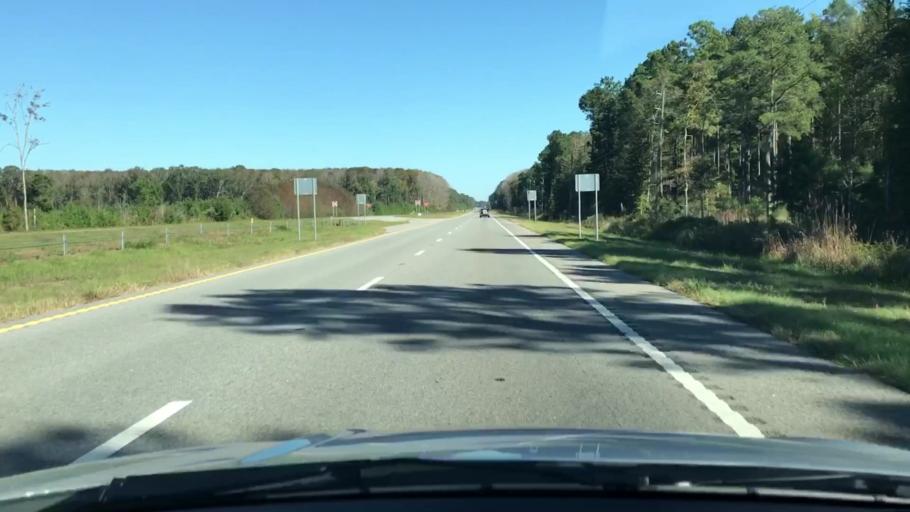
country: US
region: South Carolina
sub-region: Colleton County
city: Walterboro
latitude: 32.7677
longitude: -80.4931
